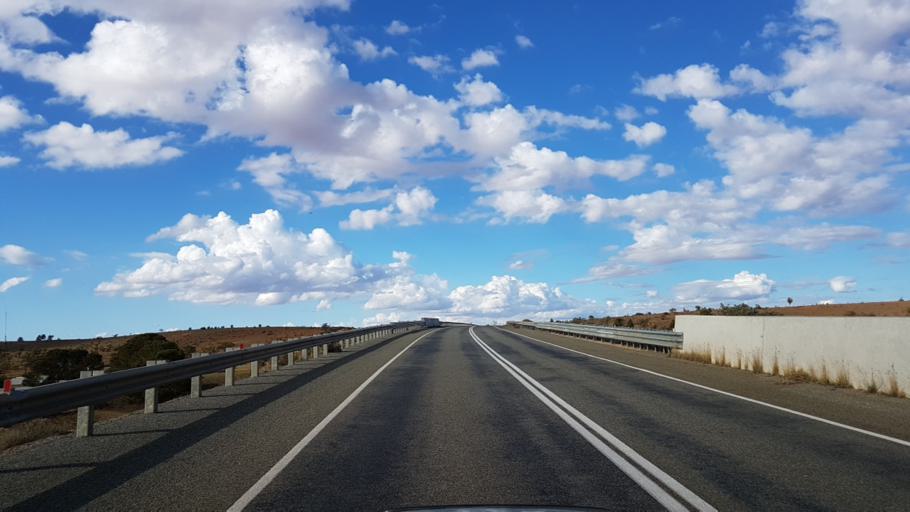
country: AU
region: South Australia
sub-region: Peterborough
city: Peterborough
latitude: -32.9543
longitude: 138.9023
